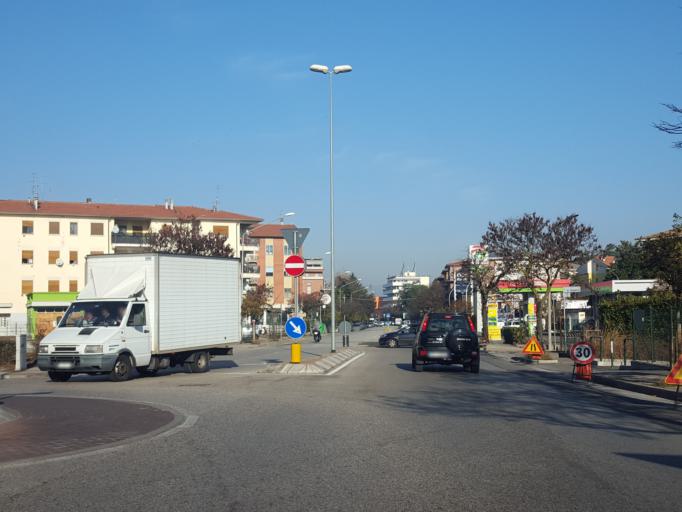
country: IT
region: Veneto
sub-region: Provincia di Vicenza
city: Vicenza
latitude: 45.5492
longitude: 11.5632
